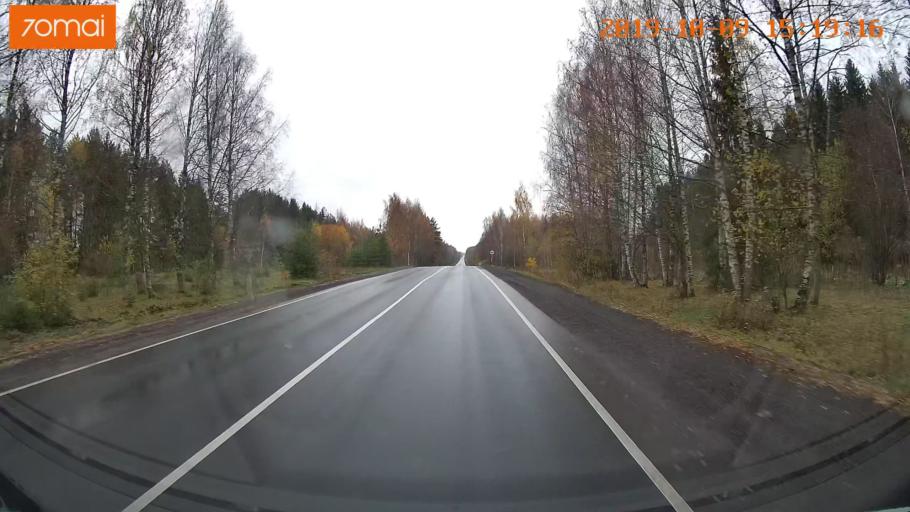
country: RU
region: Kostroma
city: Susanino
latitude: 58.0774
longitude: 41.5593
